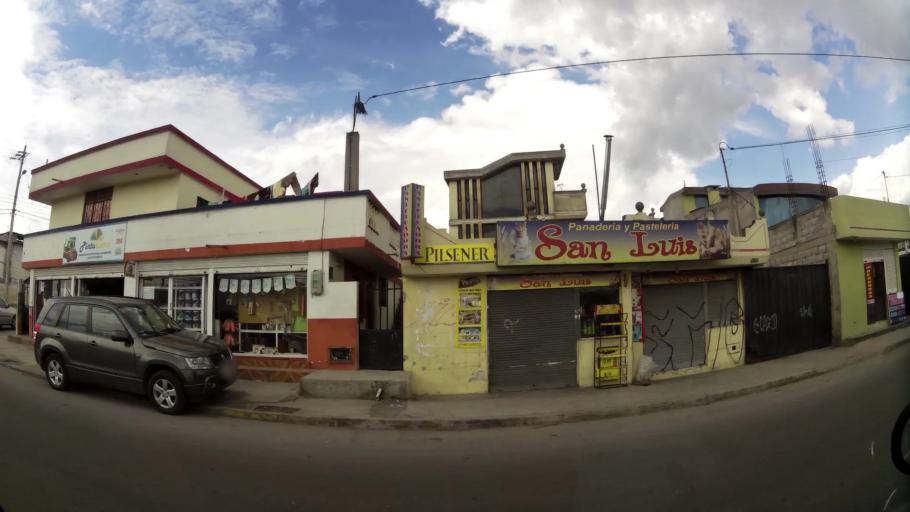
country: EC
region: Pichincha
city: Quito
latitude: -0.0970
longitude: -78.4444
